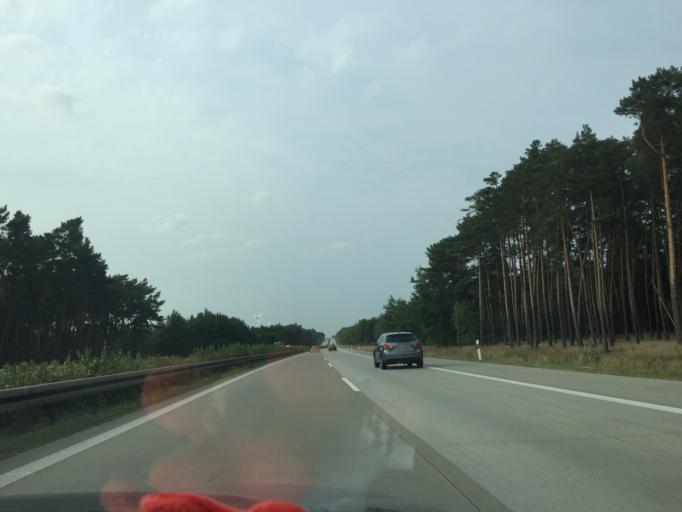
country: DE
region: Brandenburg
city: Bestensee
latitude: 52.2234
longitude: 13.5960
